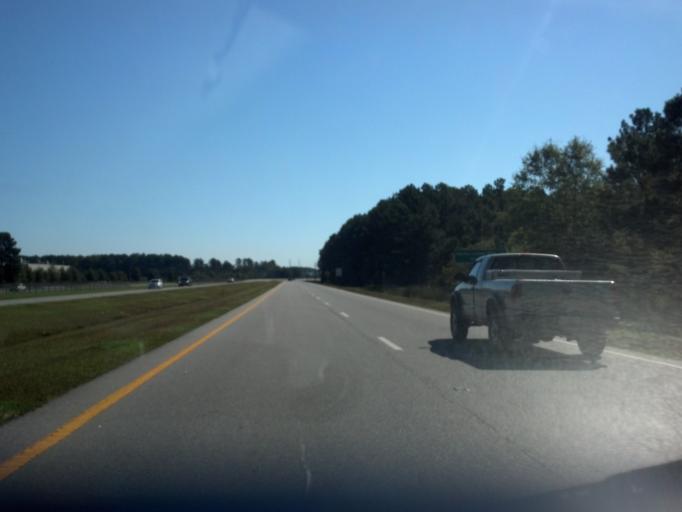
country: US
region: North Carolina
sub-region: Pitt County
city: Greenville
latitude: 35.6581
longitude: -77.3588
